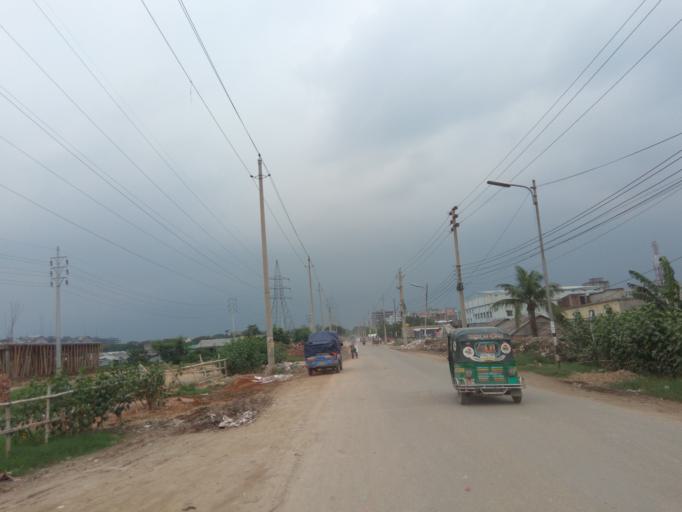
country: BD
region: Dhaka
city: Azimpur
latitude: 23.7356
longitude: 90.3618
